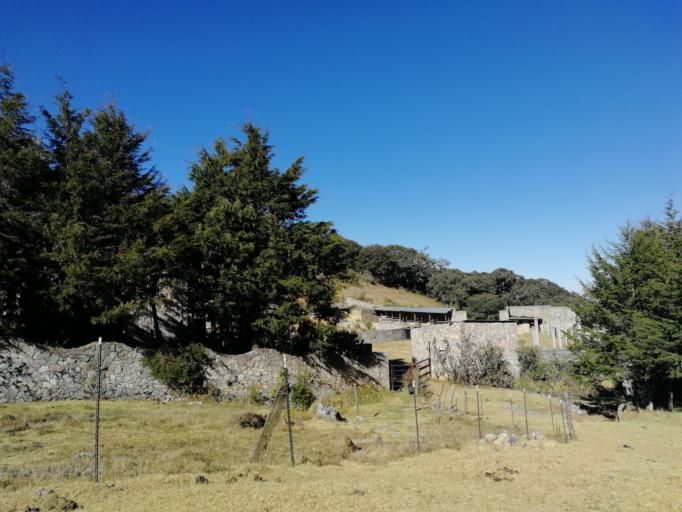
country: MX
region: San Luis Potosi
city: Zaragoza
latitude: 22.0163
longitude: -100.6106
